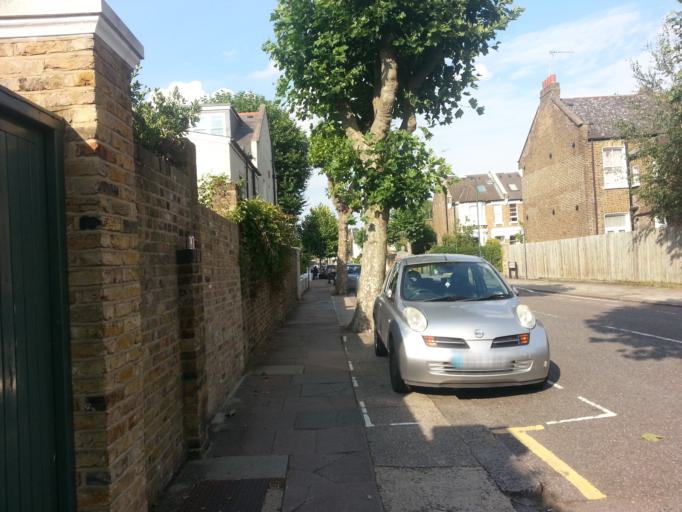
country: GB
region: England
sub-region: Greater London
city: Bayswater
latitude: 51.5363
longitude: -0.2027
